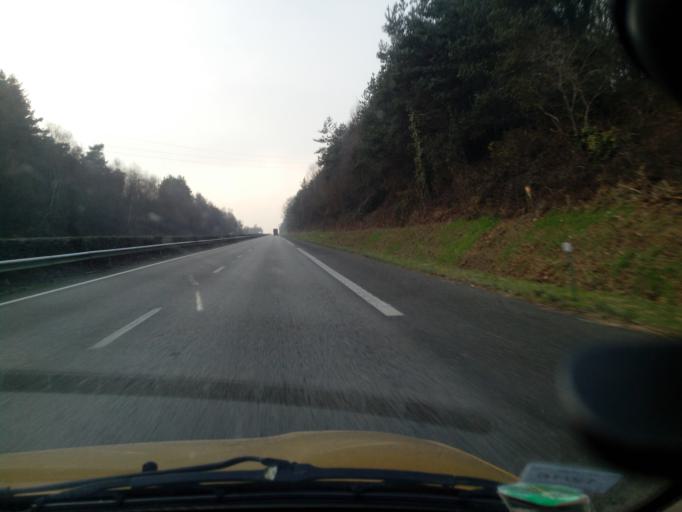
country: FR
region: Brittany
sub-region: Departement du Morbihan
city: Taupont
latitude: 47.9347
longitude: -2.4319
